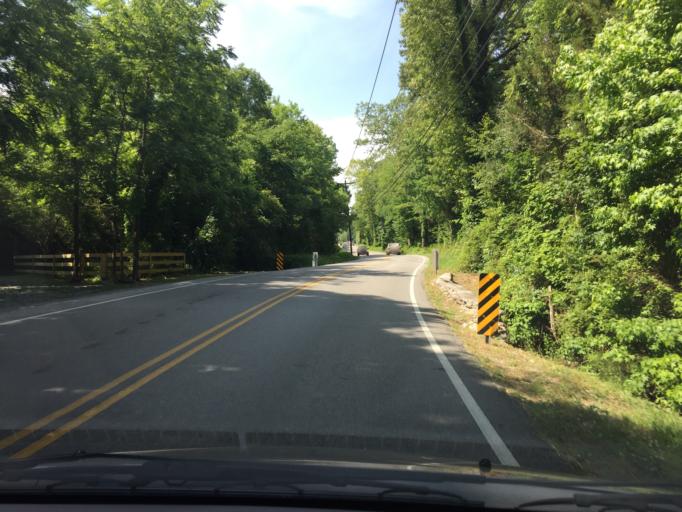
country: US
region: Tennessee
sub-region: Hamilton County
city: Collegedale
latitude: 35.0720
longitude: -85.0354
